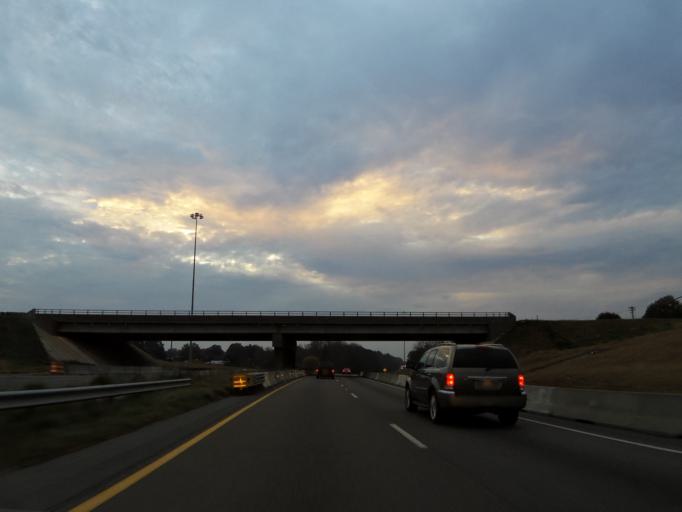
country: US
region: North Carolina
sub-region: Burke County
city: Morganton
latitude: 35.7176
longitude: -81.6716
